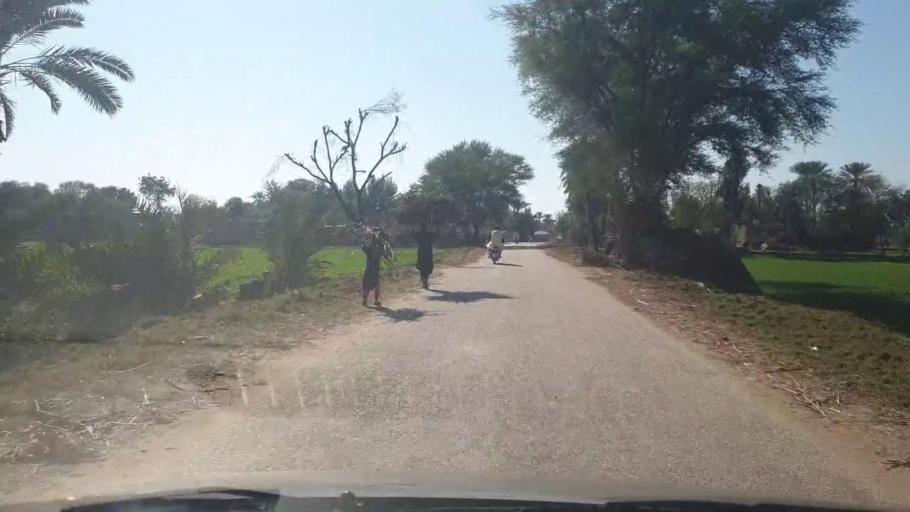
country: PK
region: Sindh
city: Bozdar
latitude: 27.1377
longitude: 68.6449
